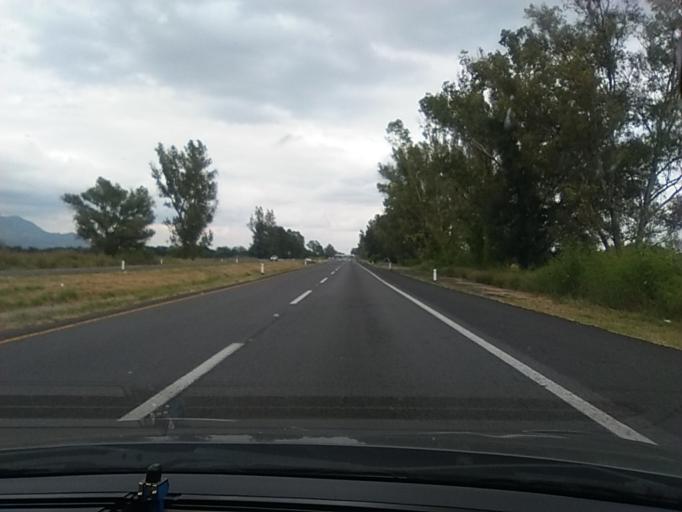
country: MX
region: Jalisco
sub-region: Ocotlan
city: Joconoxtle (La Tuna)
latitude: 20.3813
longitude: -102.6999
